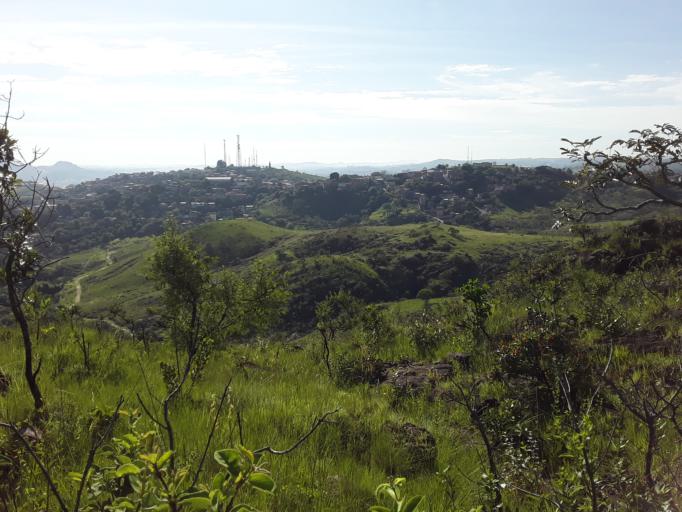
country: BR
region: Minas Gerais
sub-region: Sao Joao Del Rei
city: Sao Joao del Rei
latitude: -21.1264
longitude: -44.2754
